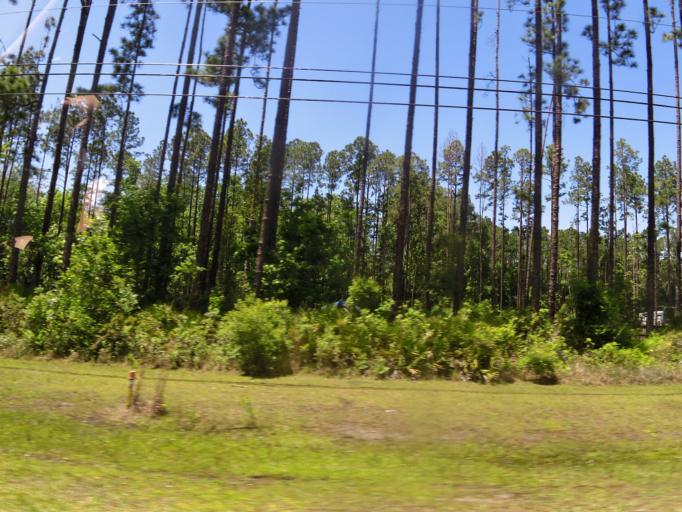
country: US
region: Florida
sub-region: Clay County
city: Green Cove Springs
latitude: 30.0291
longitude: -81.5928
